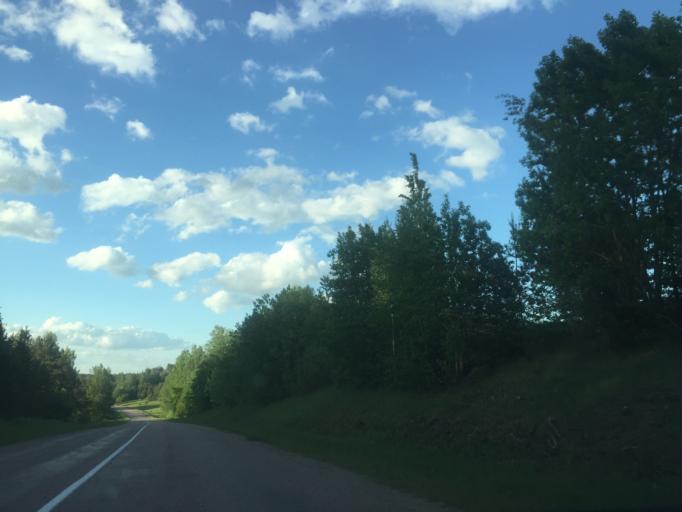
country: LV
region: Kandava
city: Kandava
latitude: 57.0176
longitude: 22.7916
